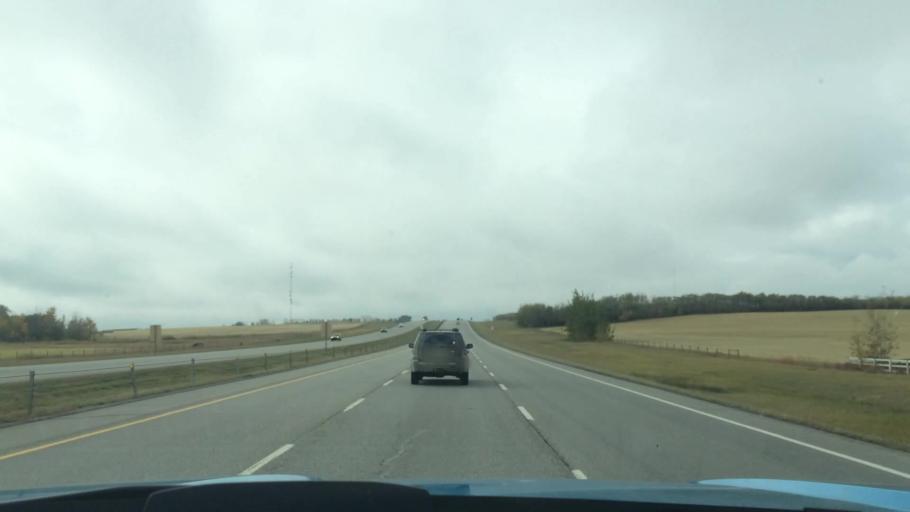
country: CA
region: Alberta
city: Penhold
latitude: 52.0730
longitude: -113.8725
